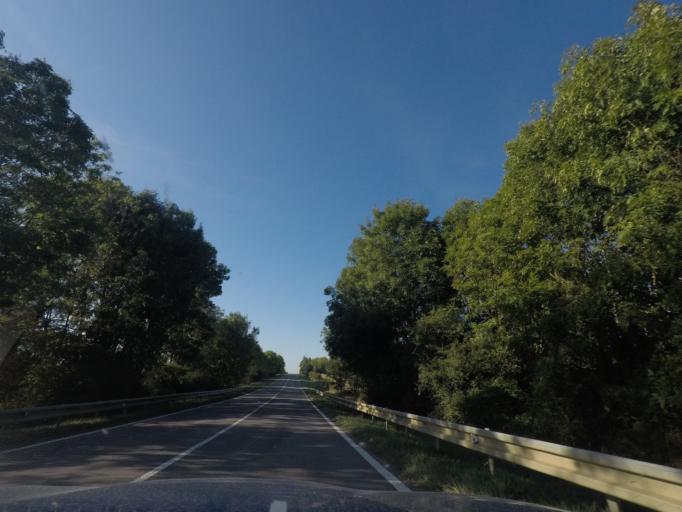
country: LU
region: Luxembourg
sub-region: Canton d'Esch-sur-Alzette
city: Frisange
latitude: 49.4755
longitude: 6.1875
